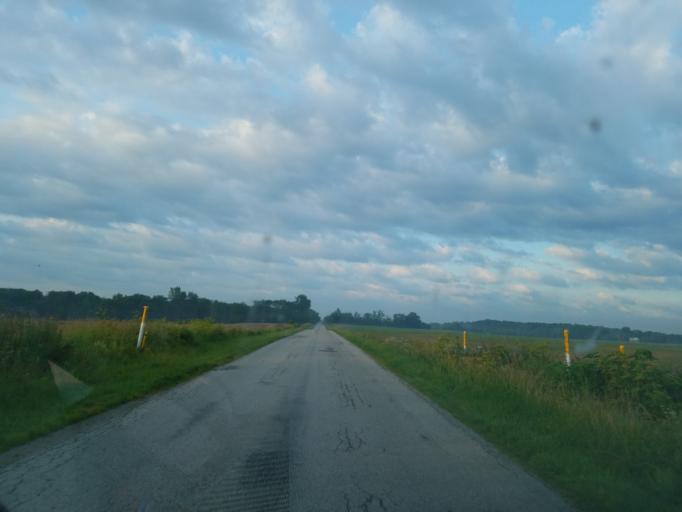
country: US
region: Ohio
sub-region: Morrow County
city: Cardington
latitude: 40.5351
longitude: -82.9194
